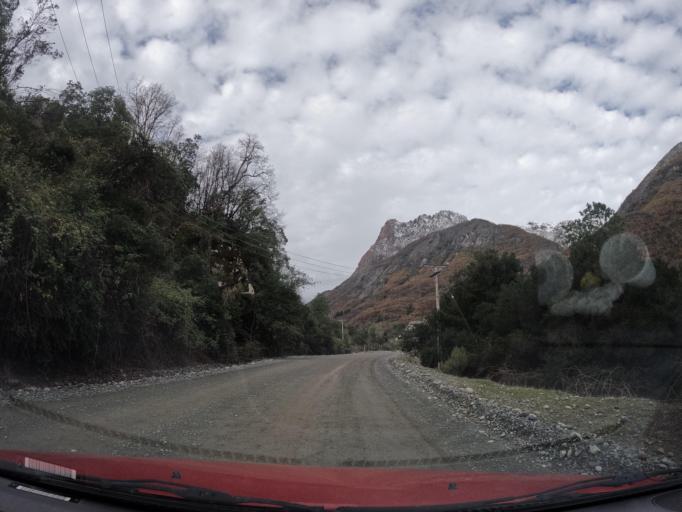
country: CL
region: Maule
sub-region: Provincia de Linares
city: Colbun
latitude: -35.8579
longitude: -71.2117
